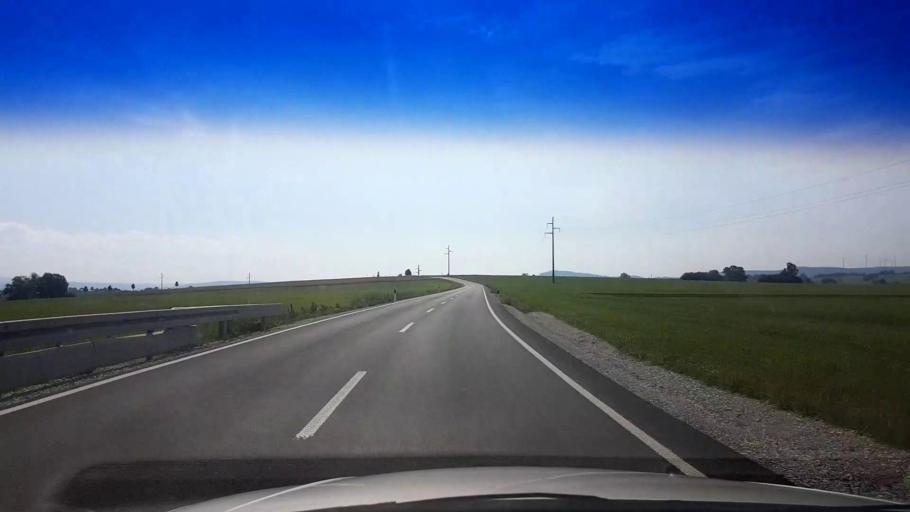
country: DE
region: Bavaria
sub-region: Upper Franconia
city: Mistelgau
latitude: 49.9379
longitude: 11.4632
